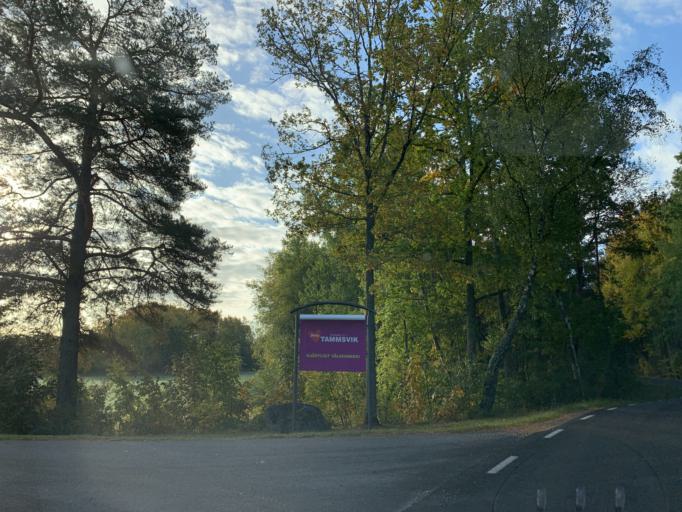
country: SE
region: Stockholm
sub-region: Upplands-Bro Kommun
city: Bro
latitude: 59.4998
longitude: 17.5898
